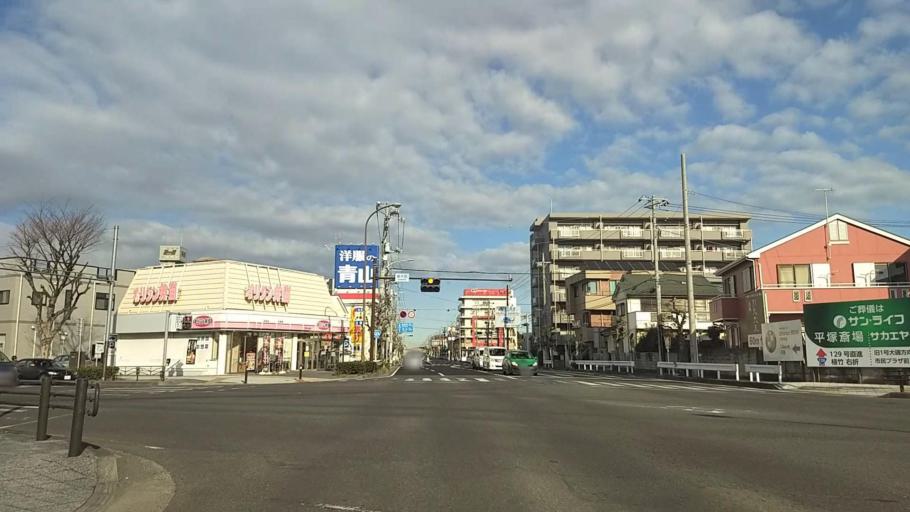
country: JP
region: Kanagawa
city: Hiratsuka
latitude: 35.3320
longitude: 139.3590
